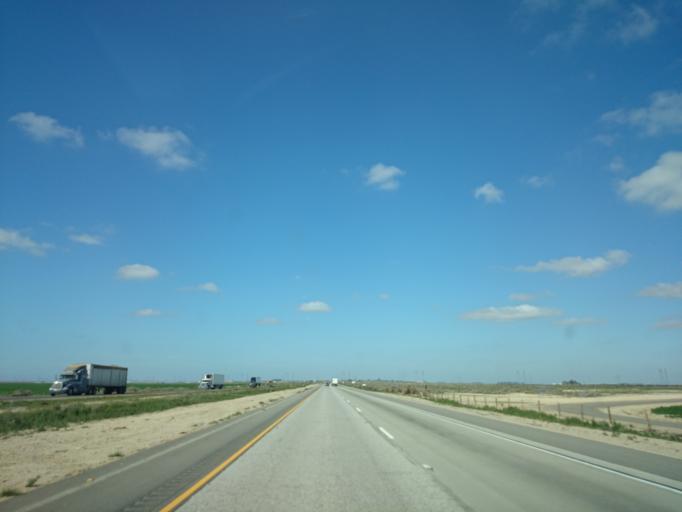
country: US
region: California
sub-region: Kern County
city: Buttonwillow
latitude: 35.3711
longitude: -119.3585
